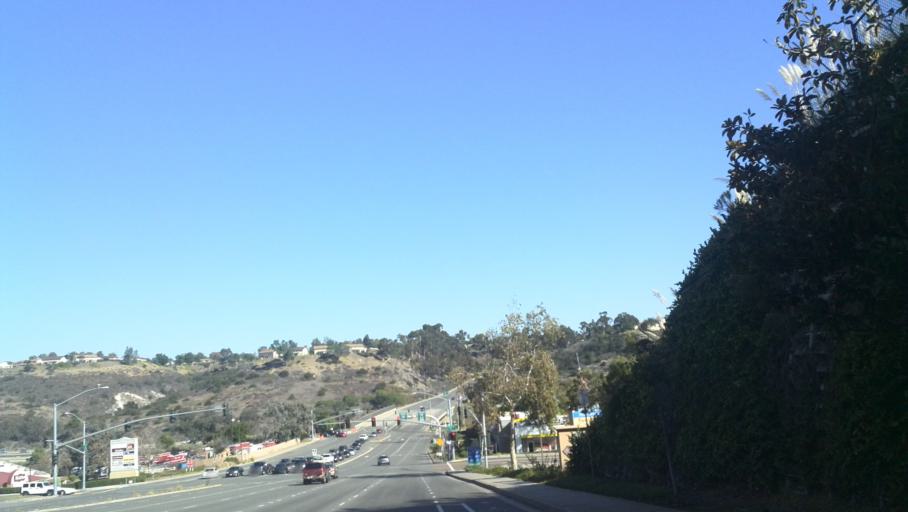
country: US
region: California
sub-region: San Diego County
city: San Diego
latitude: 32.8091
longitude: -117.1176
